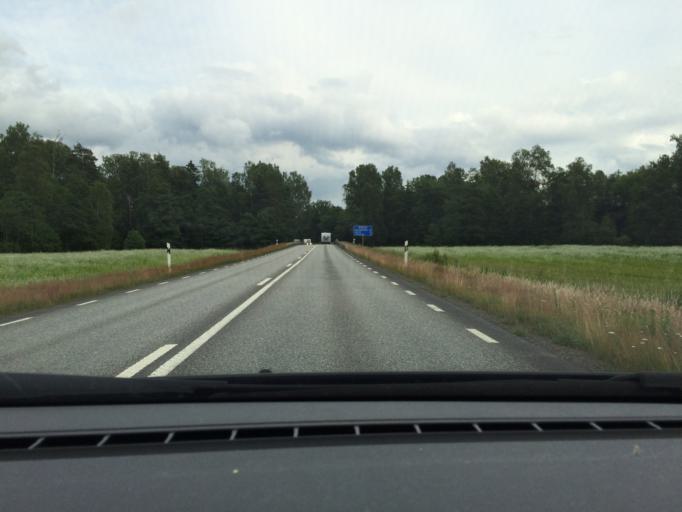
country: SE
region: Joenkoeping
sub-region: Varnamo Kommun
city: Forsheda
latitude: 57.1626
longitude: 13.8502
